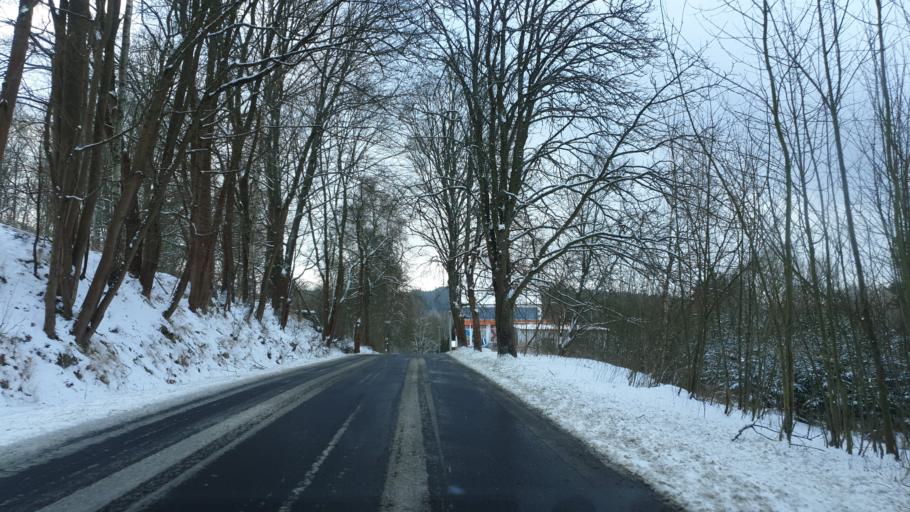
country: DE
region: Saxony
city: Bad Elster
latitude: 50.2649
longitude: 12.2447
